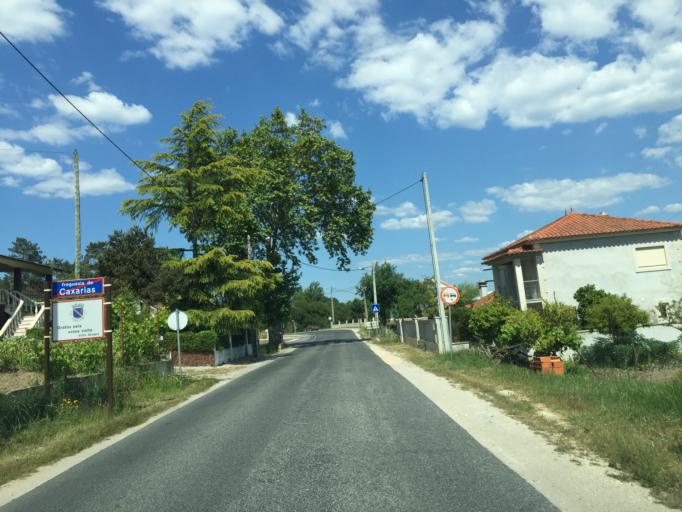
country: PT
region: Santarem
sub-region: Ourem
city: Ourem
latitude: 39.7216
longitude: -8.5151
